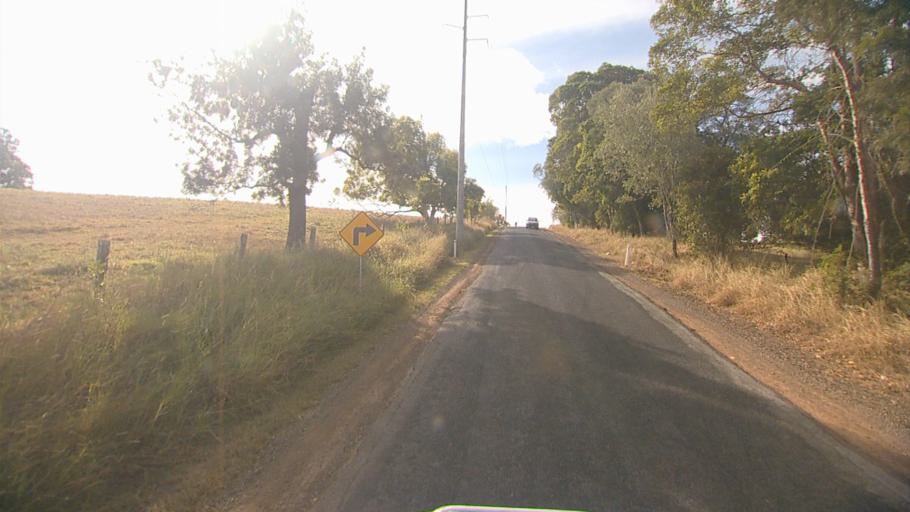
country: AU
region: Queensland
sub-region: Logan
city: Cedar Vale
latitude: -27.9019
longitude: 153.0150
